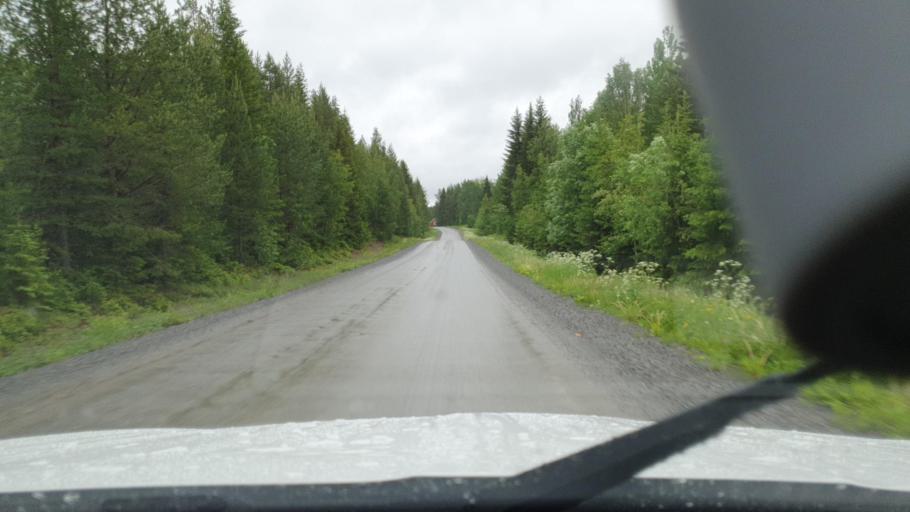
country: SE
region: Vaesterbotten
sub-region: Skelleftea Kommun
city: Burtraesk
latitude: 64.3708
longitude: 20.3790
